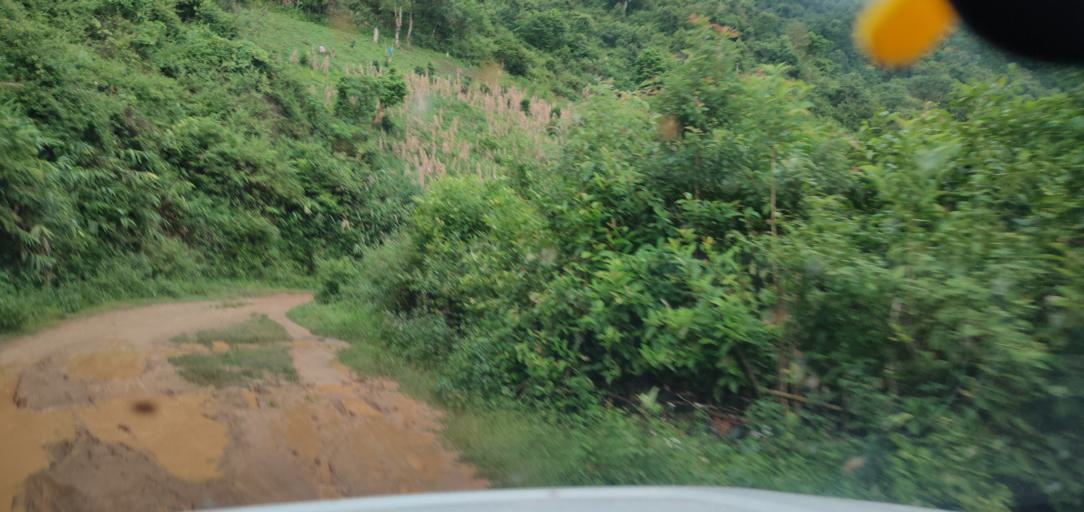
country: LA
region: Phongsali
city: Phongsali
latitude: 21.4470
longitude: 102.2911
